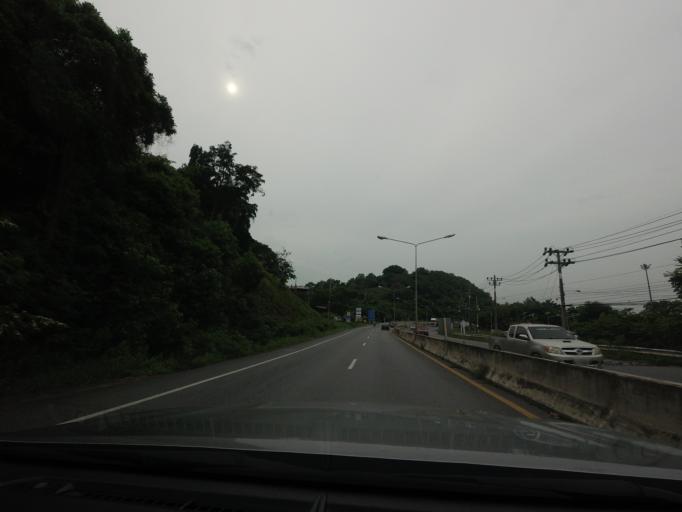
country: TH
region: Songkhla
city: Ban Mai
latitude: 7.1774
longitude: 100.5449
